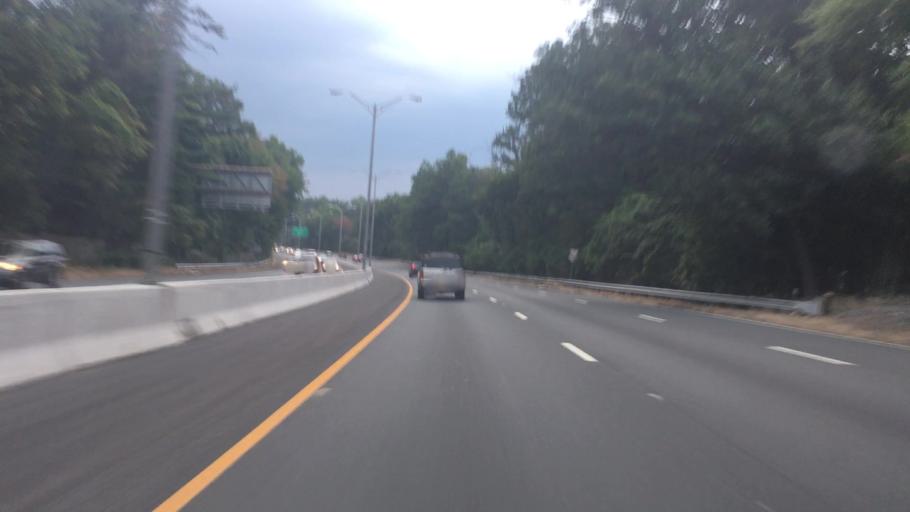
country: US
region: New Jersey
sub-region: Bergen County
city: Midland Park
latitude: 40.9813
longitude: -74.1612
